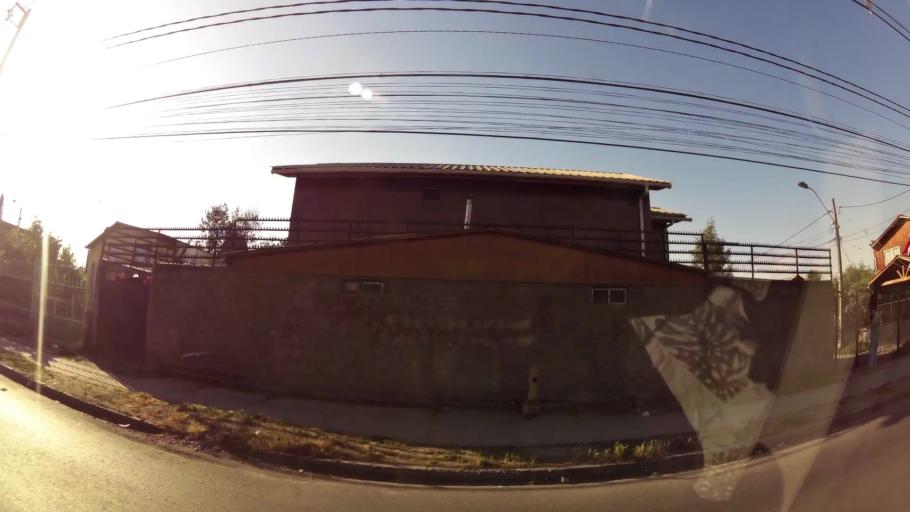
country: CL
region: Santiago Metropolitan
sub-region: Provincia de Santiago
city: La Pintana
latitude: -33.5568
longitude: -70.6256
